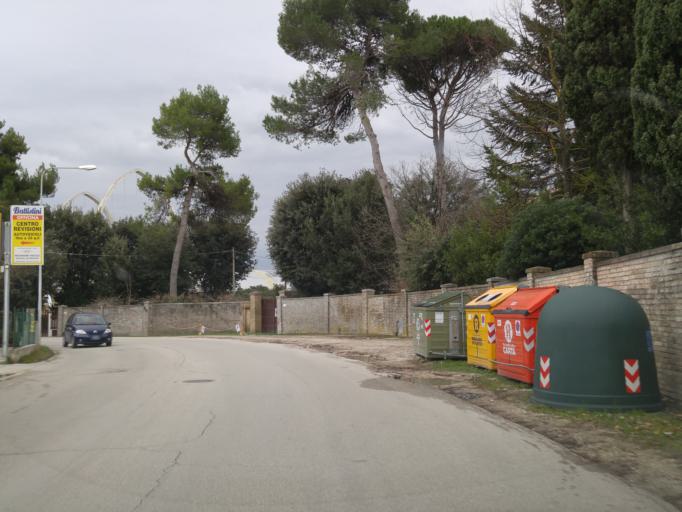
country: IT
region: The Marches
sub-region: Provincia di Pesaro e Urbino
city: Centinarola
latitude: 43.8380
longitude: 13.0001
